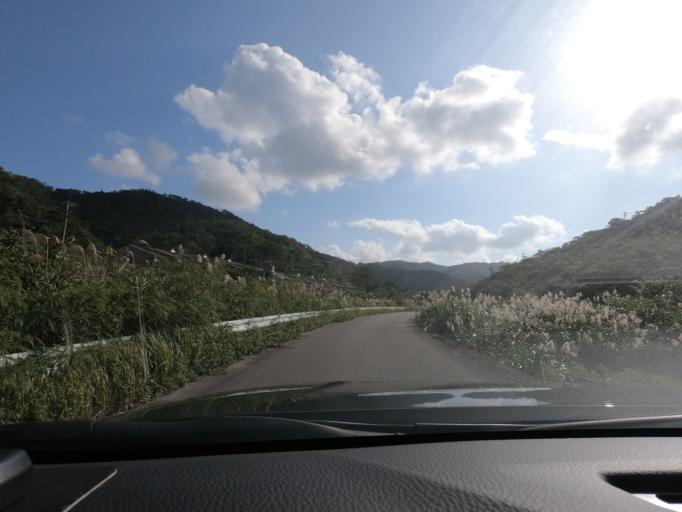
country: JP
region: Okinawa
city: Nago
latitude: 26.7663
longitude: 128.2091
